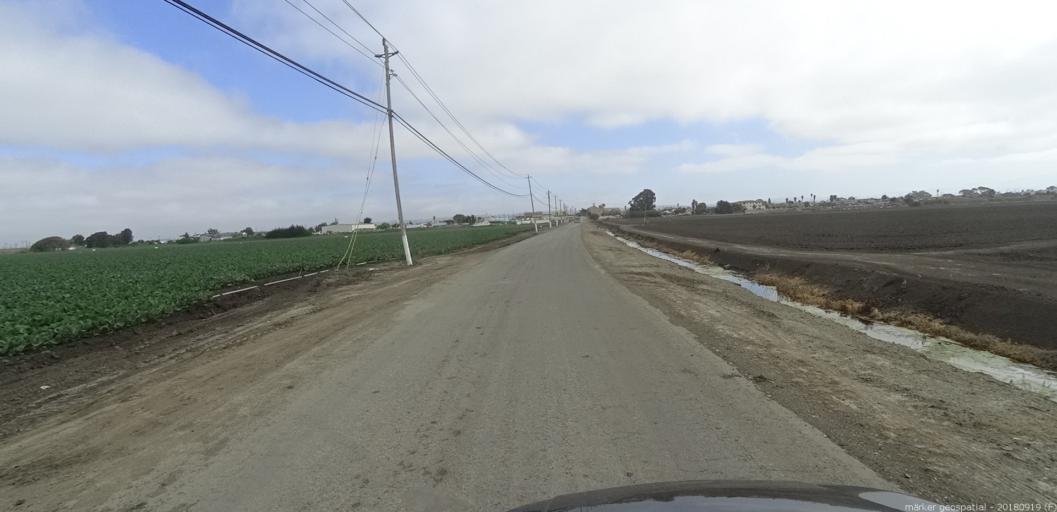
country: US
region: California
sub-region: Monterey County
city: Castroville
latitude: 36.7620
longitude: -121.7633
